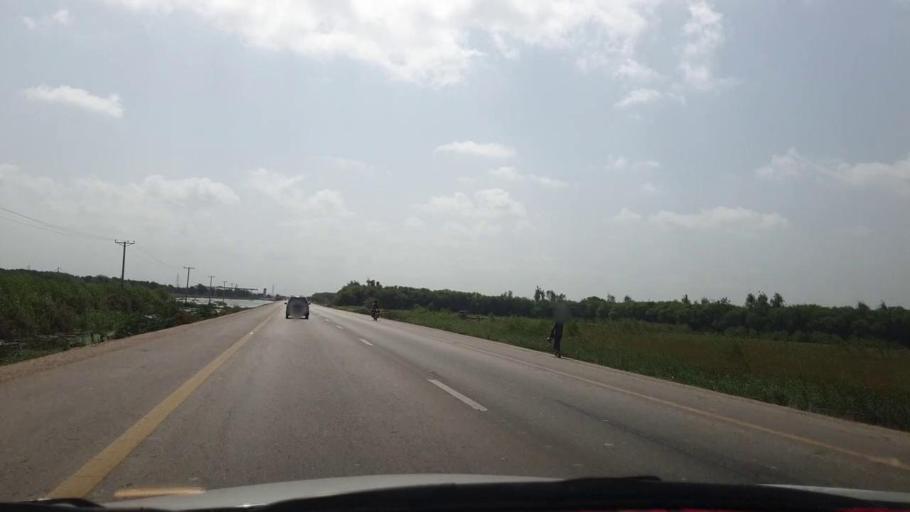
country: PK
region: Sindh
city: Talhar
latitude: 24.9346
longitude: 68.7097
